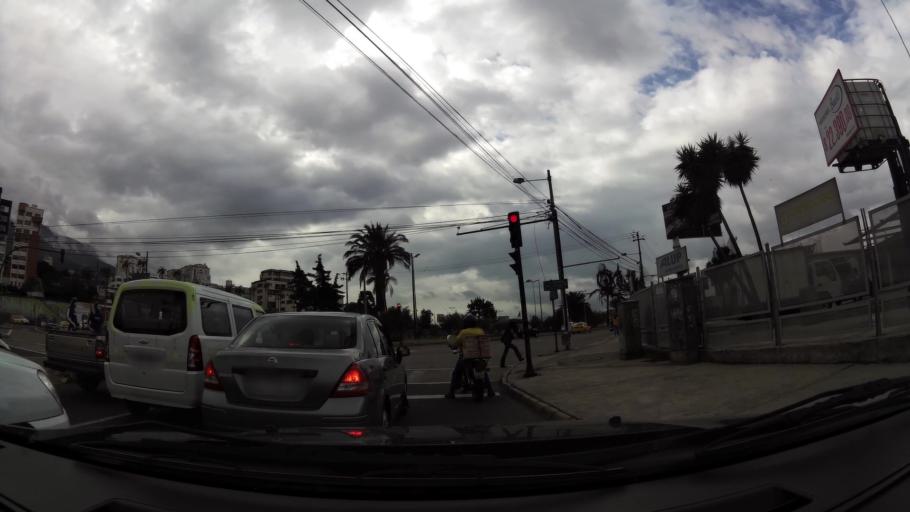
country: EC
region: Pichincha
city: Quito
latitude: -0.1686
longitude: -78.4865
